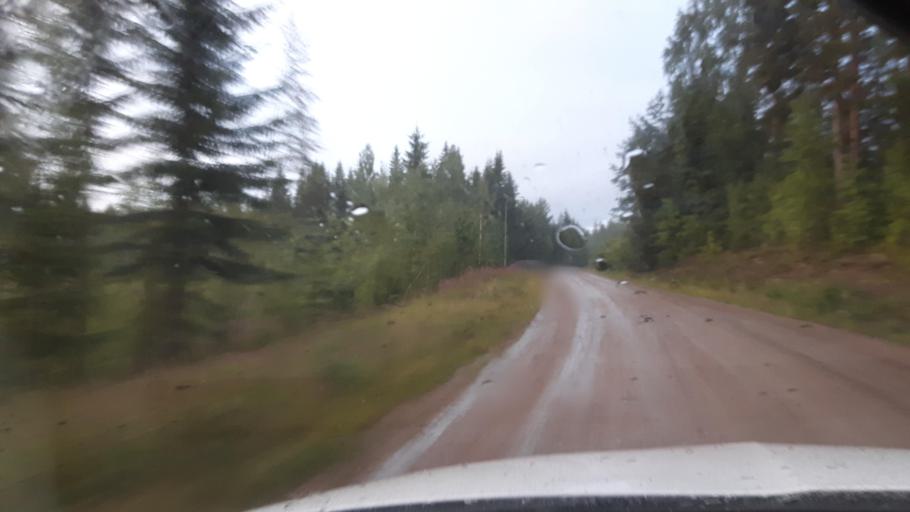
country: SE
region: Vaesternorrland
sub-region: Ange Kommun
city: Ange
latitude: 62.1414
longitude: 15.6611
